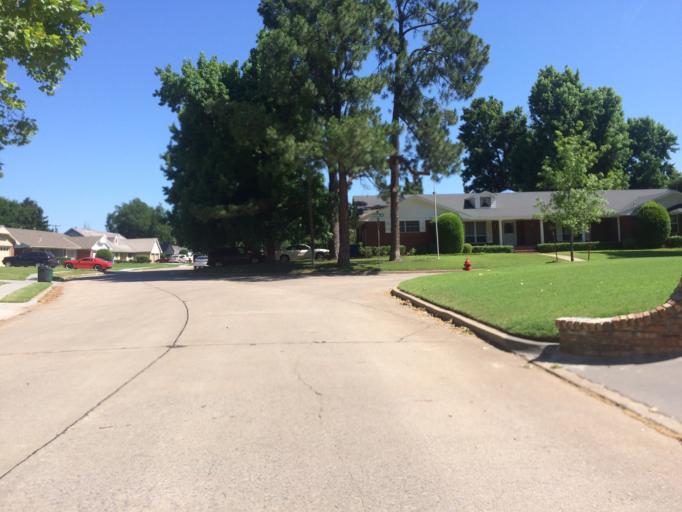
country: US
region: Oklahoma
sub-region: Cleveland County
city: Norman
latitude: 35.2218
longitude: -97.4671
